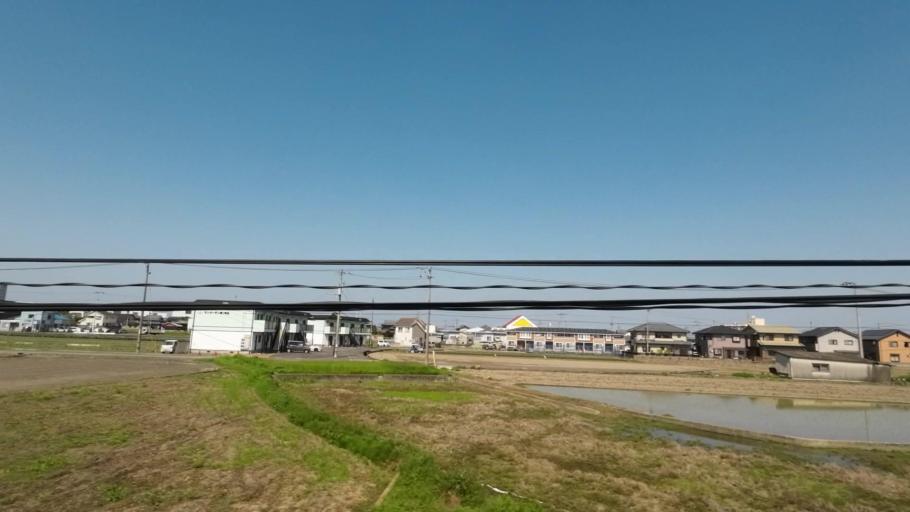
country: JP
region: Kagawa
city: Kan'onjicho
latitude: 34.1198
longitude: 133.6475
